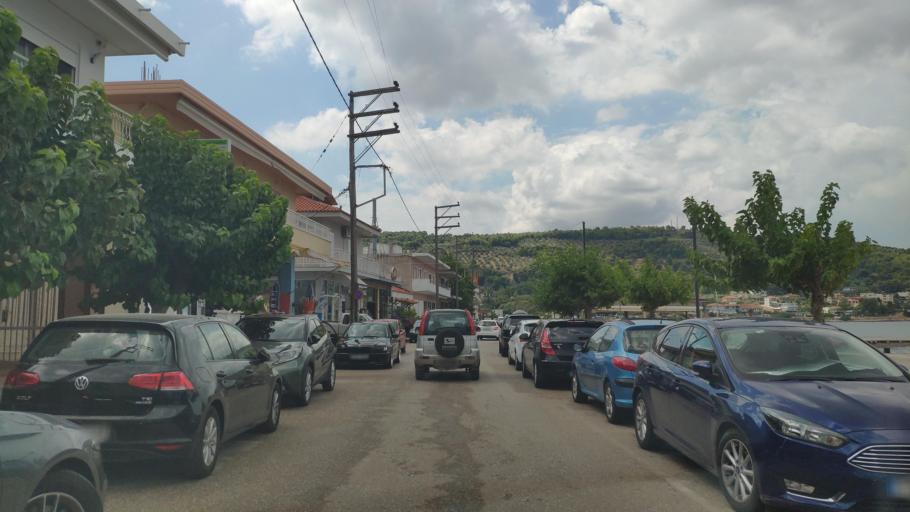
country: GR
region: Central Greece
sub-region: Nomos Fthiotidos
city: Malesina
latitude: 38.6538
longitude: 23.1927
